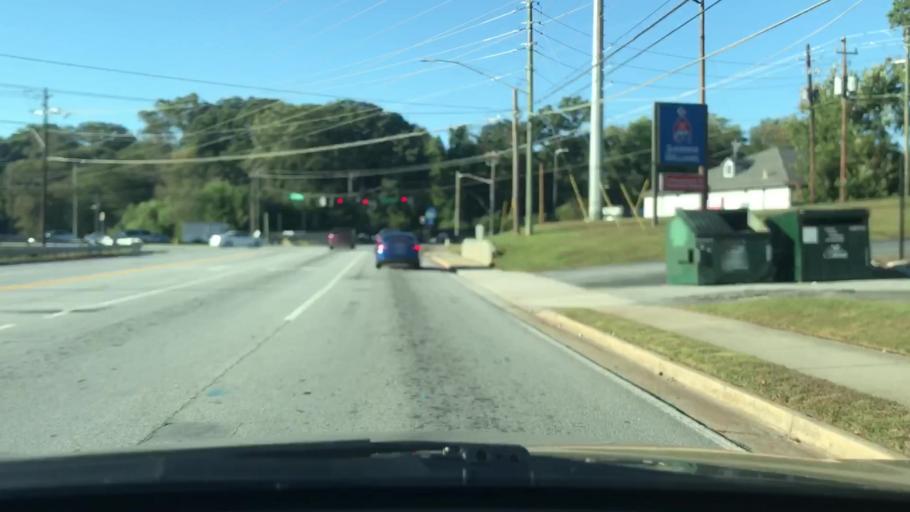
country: US
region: Georgia
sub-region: DeKalb County
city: Scottdale
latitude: 33.7995
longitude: -84.2803
